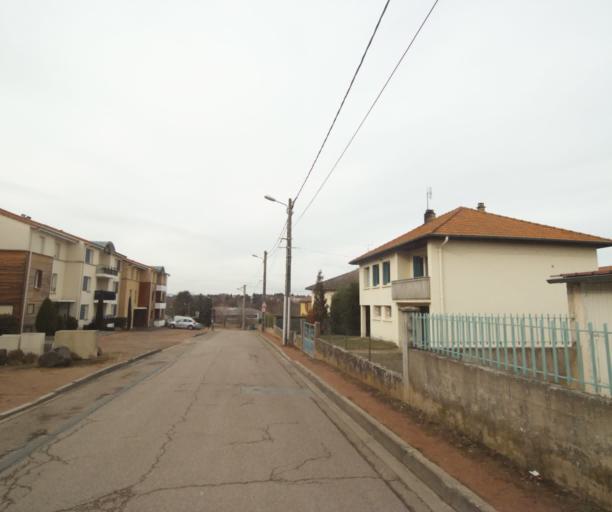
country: FR
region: Rhone-Alpes
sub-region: Departement de la Loire
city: Riorges
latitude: 46.0295
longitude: 4.0526
